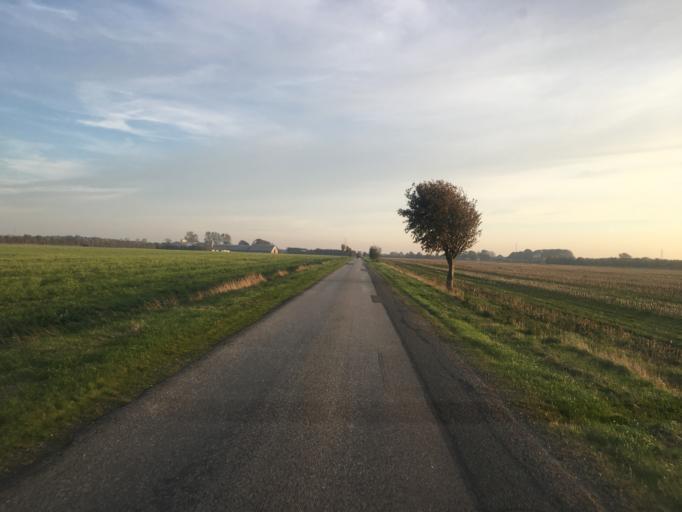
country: DK
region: South Denmark
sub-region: Tonder Kommune
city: Logumkloster
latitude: 55.0476
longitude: 9.0250
